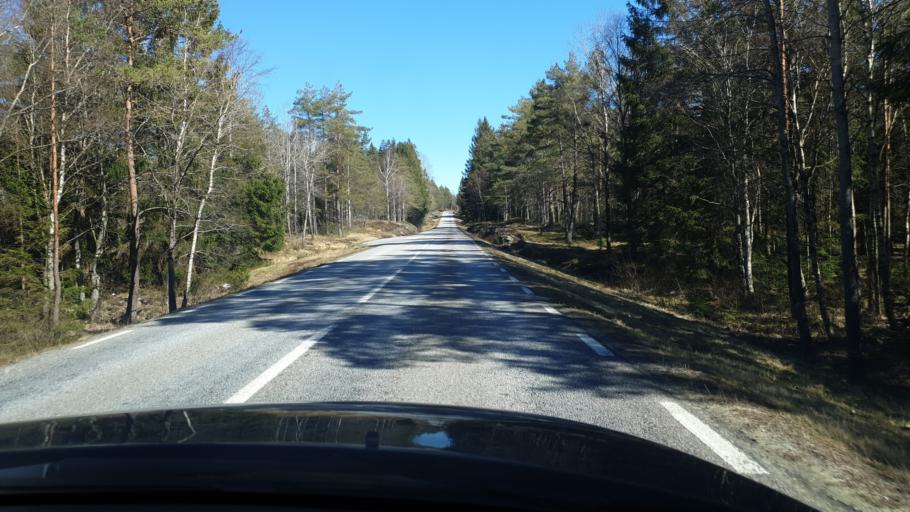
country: SE
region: Vaestra Goetaland
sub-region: Tanums Kommun
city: Tanumshede
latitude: 58.7386
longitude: 11.4496
